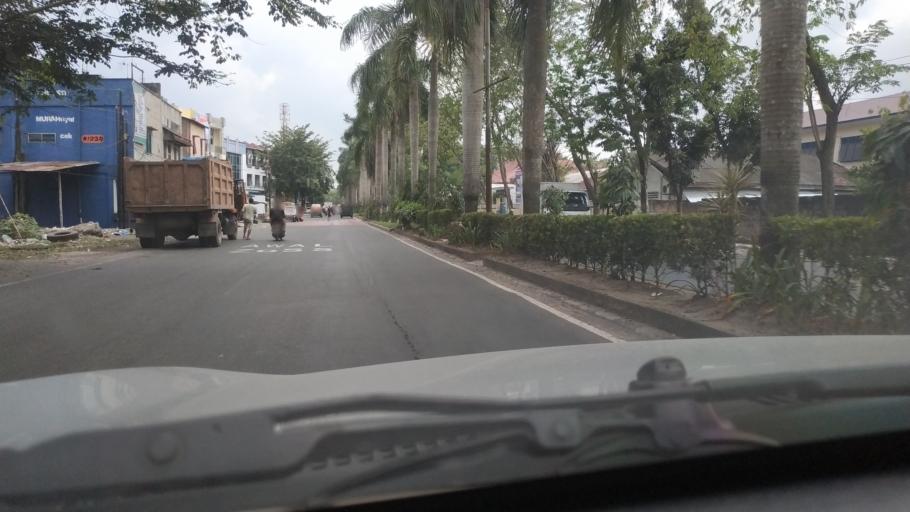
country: ID
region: North Sumatra
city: Sunggal
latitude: 3.5876
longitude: 98.6122
